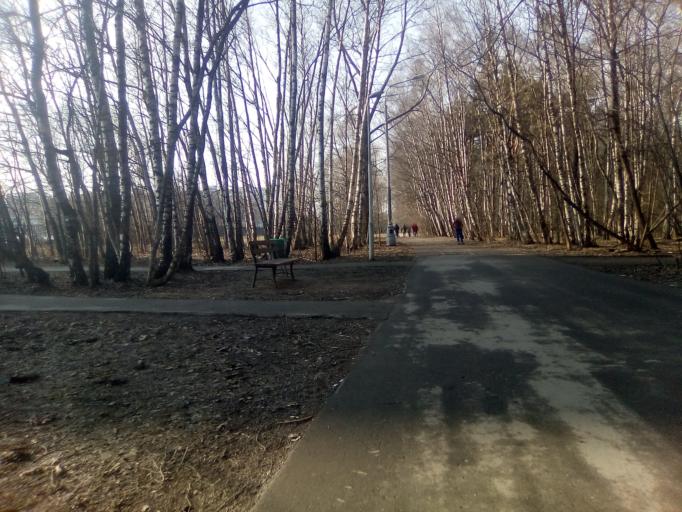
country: RU
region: Moscow
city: Tyoply Stan
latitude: 55.6354
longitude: 37.4811
